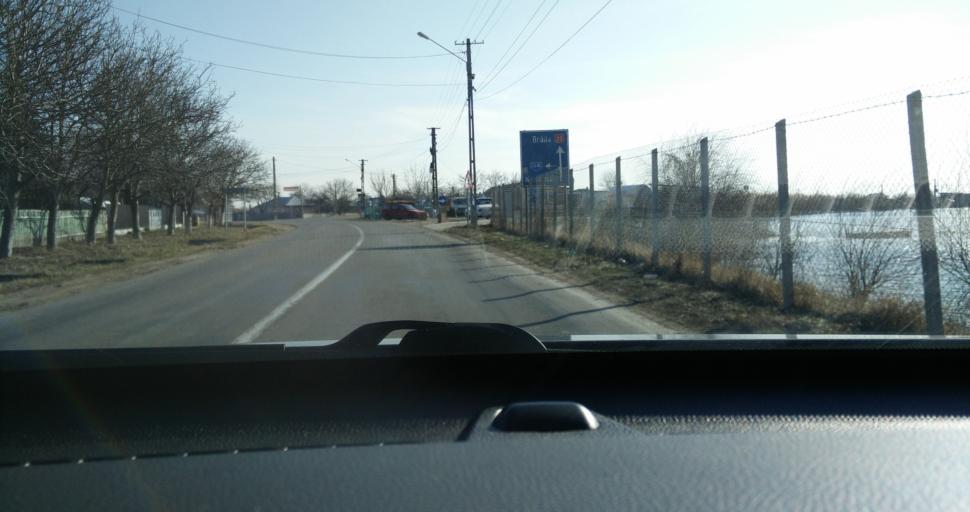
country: RO
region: Vrancea
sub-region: Comuna Nanesti
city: Nanesti
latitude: 45.5348
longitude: 27.4984
